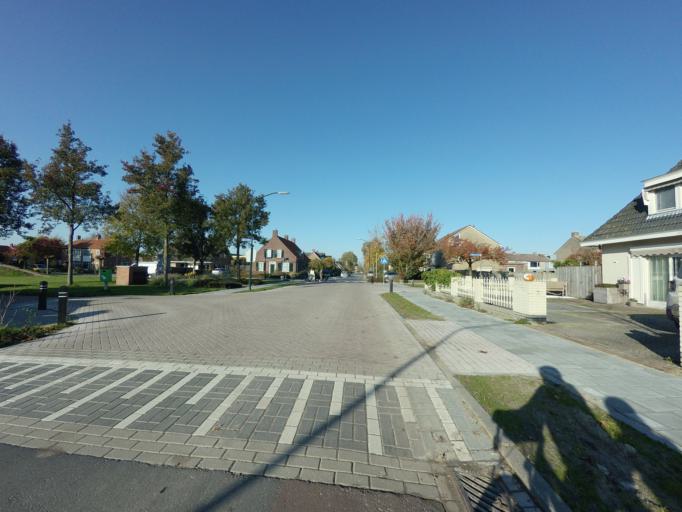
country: NL
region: North Brabant
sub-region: Gemeente Waalwijk
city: Waalwijk
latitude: 51.7306
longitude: 5.0541
